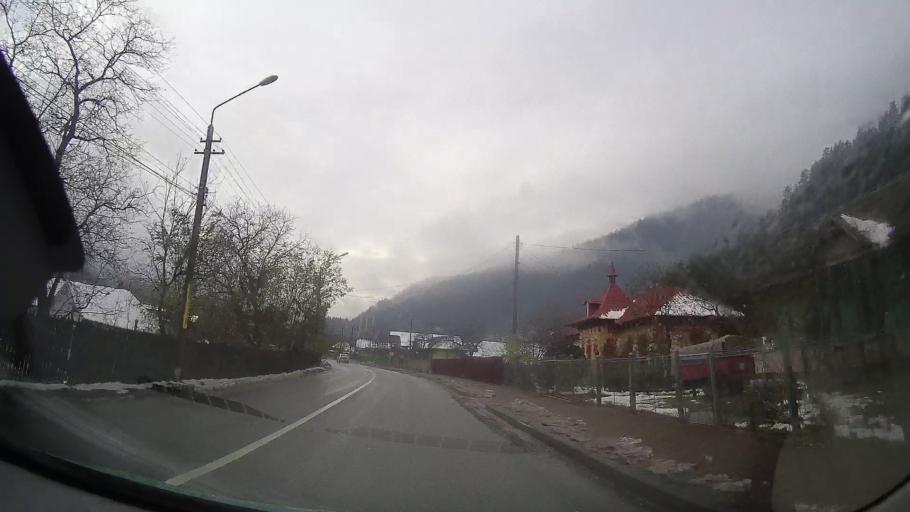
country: RO
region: Neamt
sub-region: Comuna Bicaz
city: Bicaz
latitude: 46.9098
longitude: 26.0826
